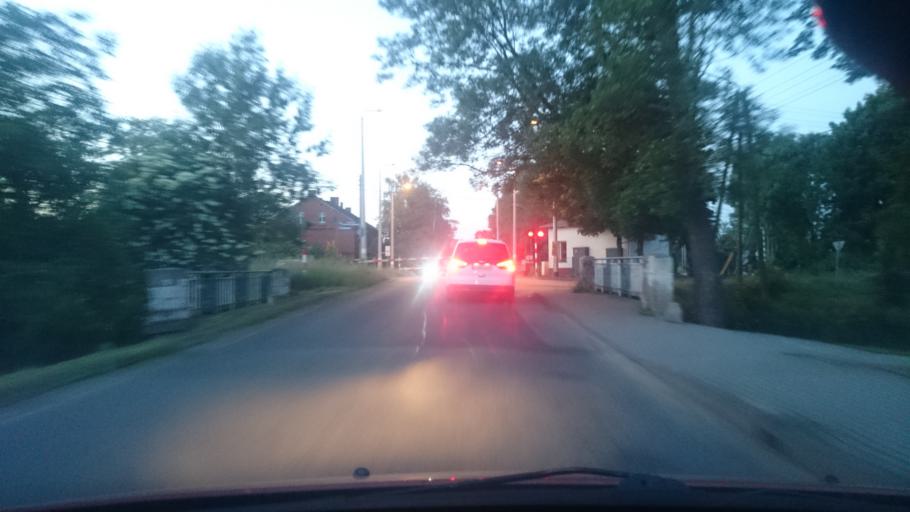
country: PL
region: Opole Voivodeship
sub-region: Powiat opolski
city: Ozimek
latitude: 50.6700
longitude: 18.2020
